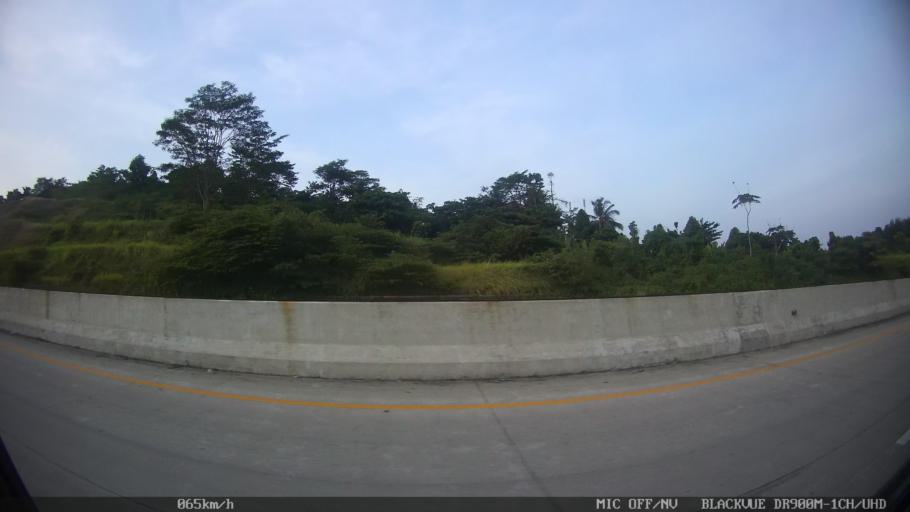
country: ID
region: Lampung
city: Penengahan
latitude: -5.8628
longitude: 105.7404
